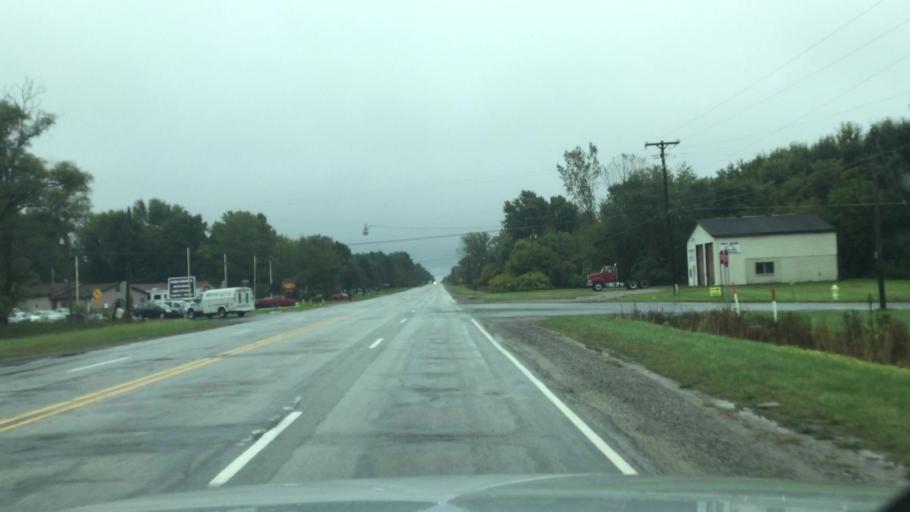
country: US
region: Michigan
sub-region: Saginaw County
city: Bridgeport
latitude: 43.3220
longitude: -83.8238
